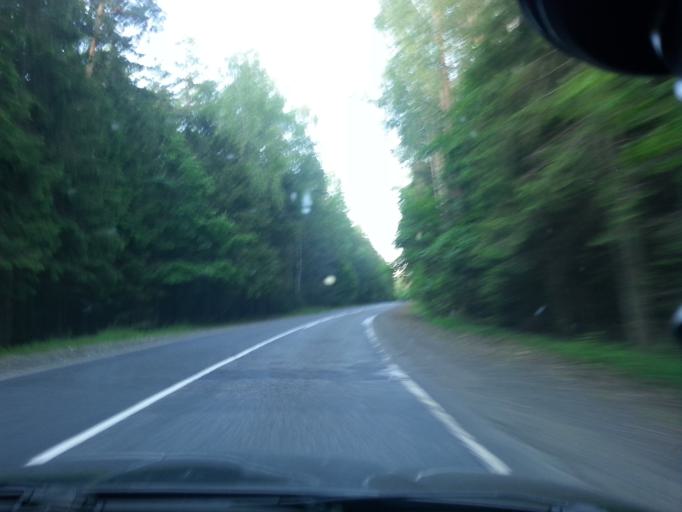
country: BY
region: Minsk
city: Svir
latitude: 54.9242
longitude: 26.5302
